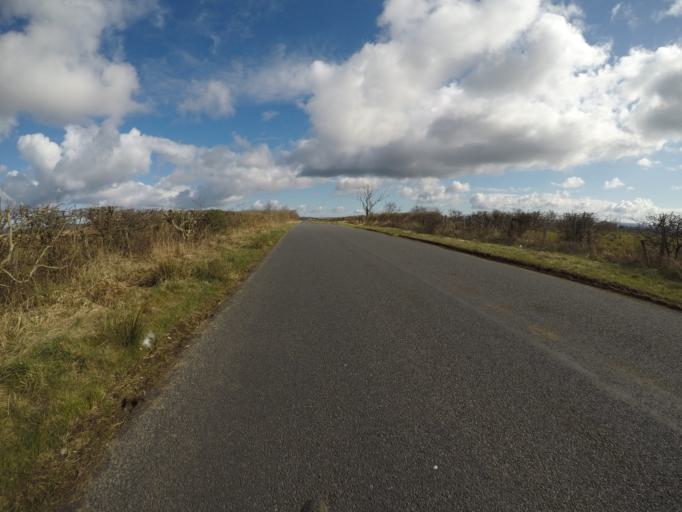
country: GB
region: Scotland
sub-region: North Ayrshire
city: Kilwinning
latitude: 55.6802
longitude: -4.6532
